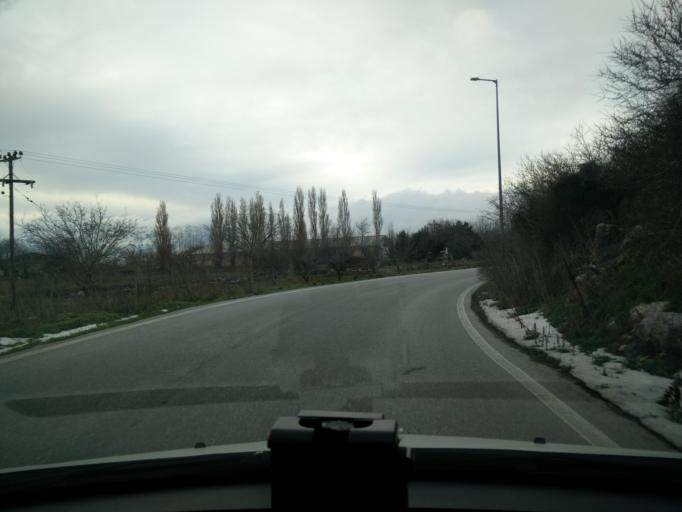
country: GR
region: Crete
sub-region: Nomos Irakleiou
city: Malia
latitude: 35.1920
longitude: 25.4919
